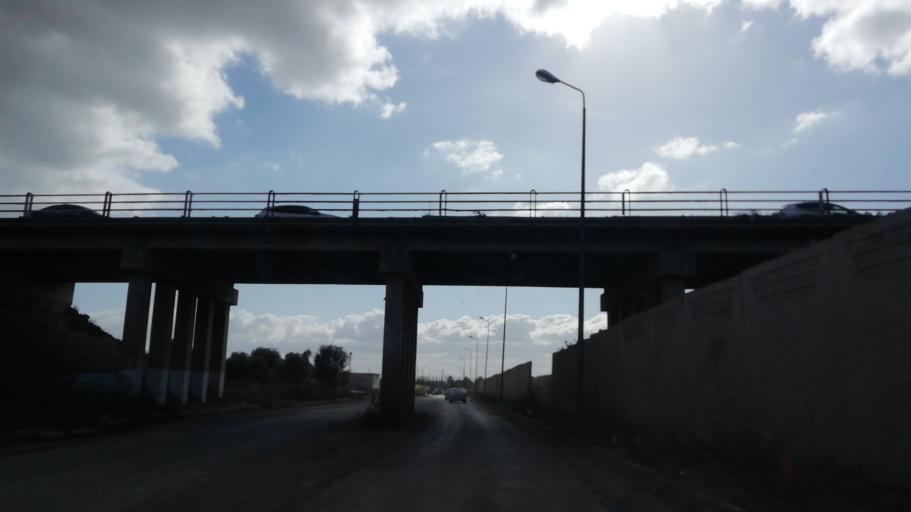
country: DZ
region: Oran
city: Es Senia
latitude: 35.6242
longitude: -0.5893
